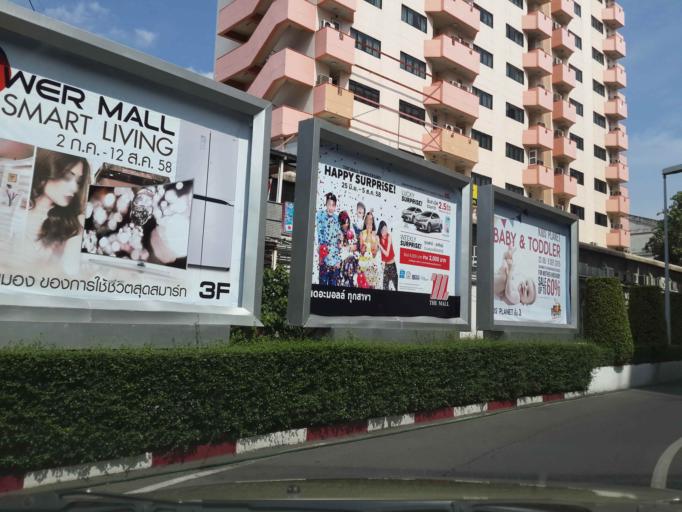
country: TH
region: Bangkok
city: Bang Kapi
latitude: 13.7669
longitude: 100.6433
